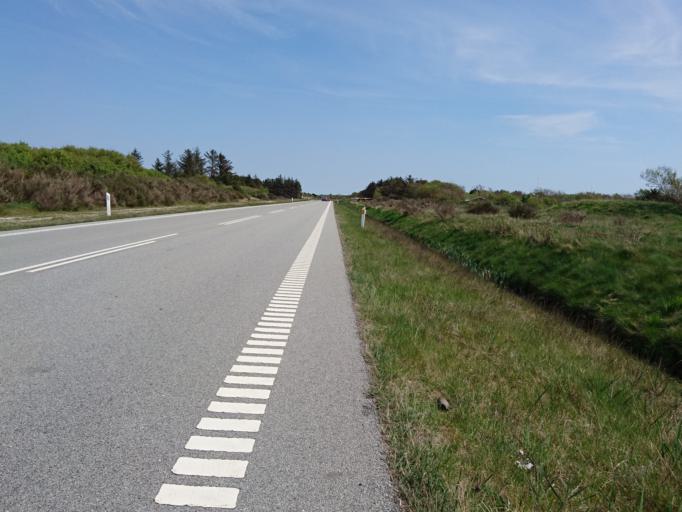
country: DK
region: North Denmark
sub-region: Frederikshavn Kommune
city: Skagen
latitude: 57.7381
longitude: 10.5878
